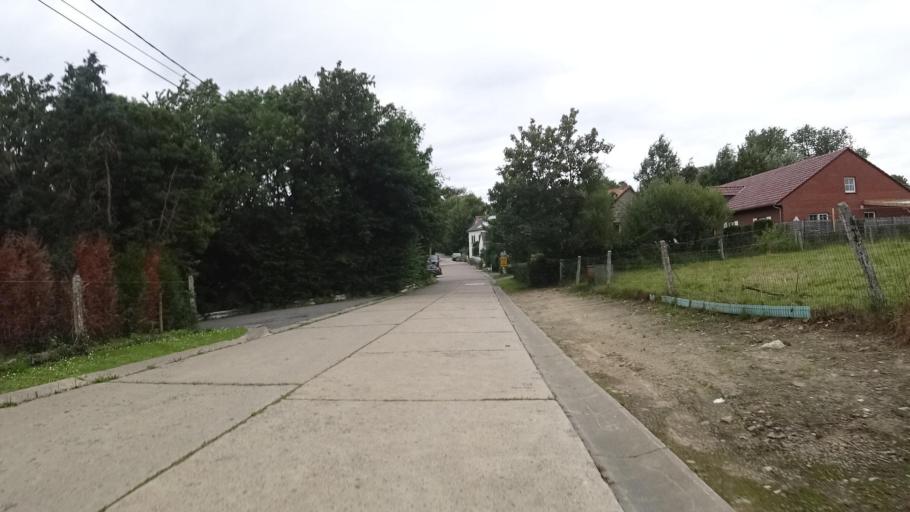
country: BE
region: Wallonia
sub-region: Province du Brabant Wallon
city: Chastre-Villeroux-Blanmont
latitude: 50.6321
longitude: 4.6514
